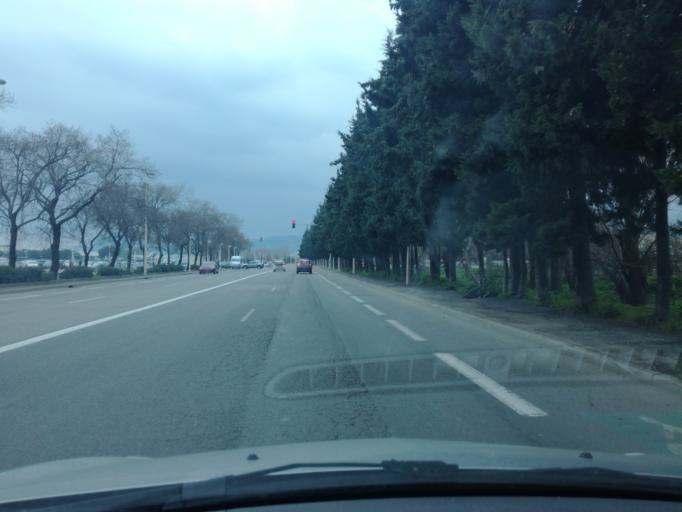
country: FR
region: Provence-Alpes-Cote d'Azur
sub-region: Departement des Alpes-Maritimes
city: Mandelieu-la-Napoule
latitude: 43.5534
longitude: 6.9635
